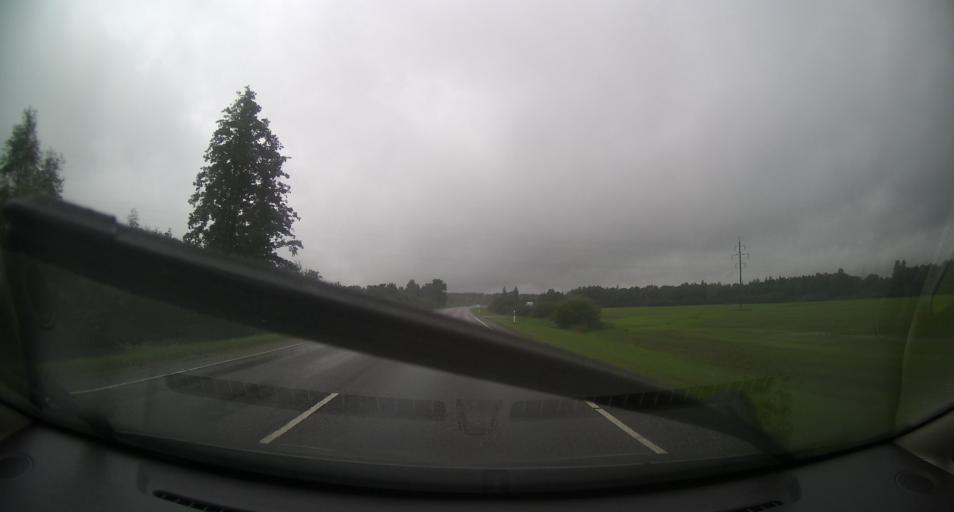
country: EE
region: Laeaene
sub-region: Lihula vald
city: Lihula
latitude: 58.6734
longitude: 23.7738
